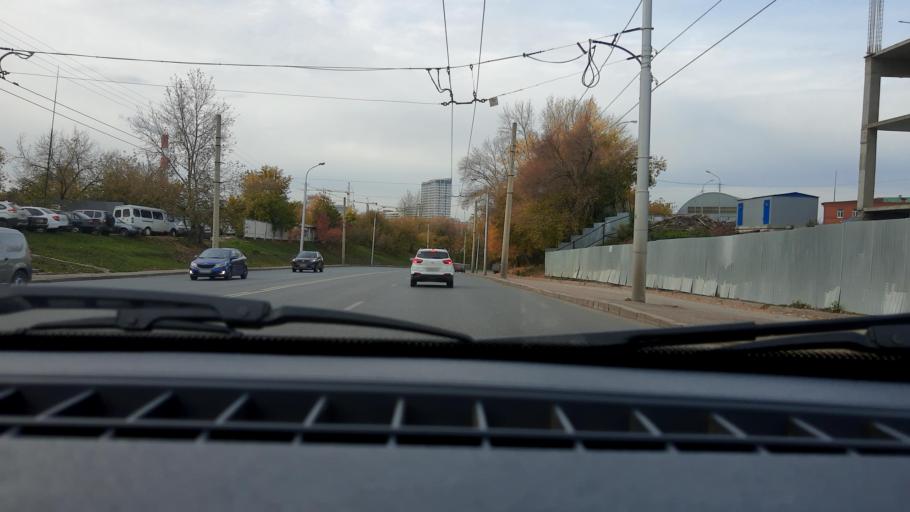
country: RU
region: Bashkortostan
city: Ufa
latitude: 54.7503
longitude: 55.9795
